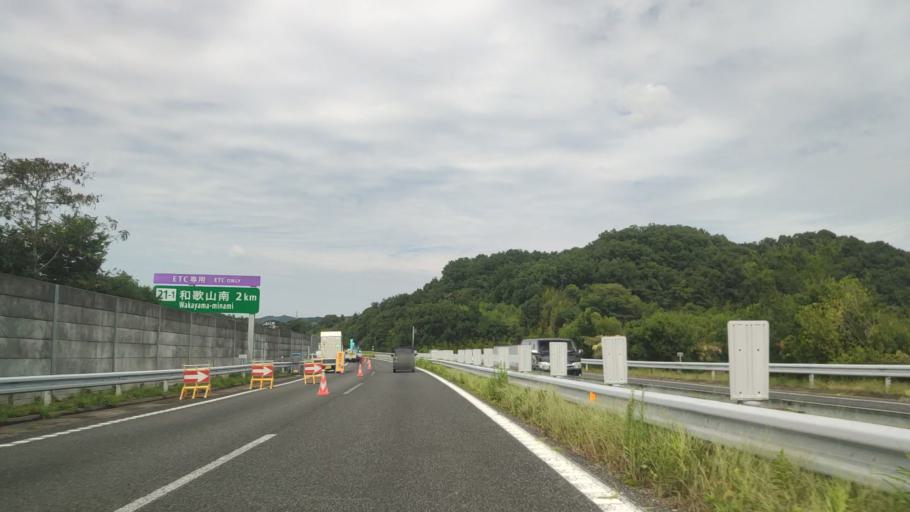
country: JP
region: Wakayama
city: Kainan
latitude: 34.1902
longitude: 135.2384
